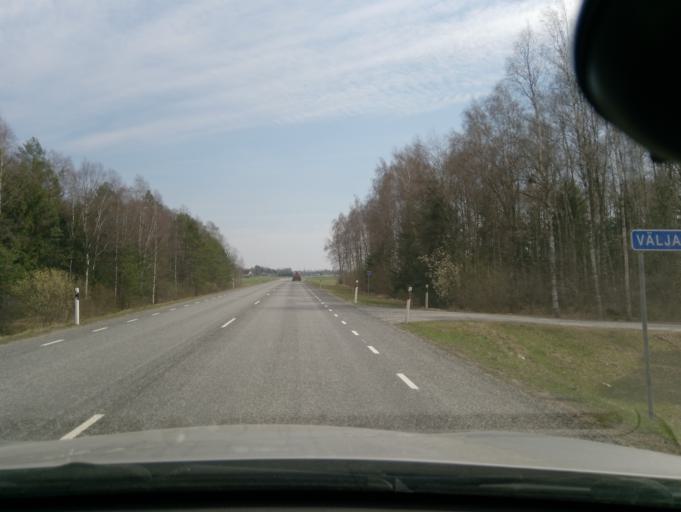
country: EE
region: Jaervamaa
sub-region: Tueri vald
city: Sarevere
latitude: 58.7657
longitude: 25.5358
